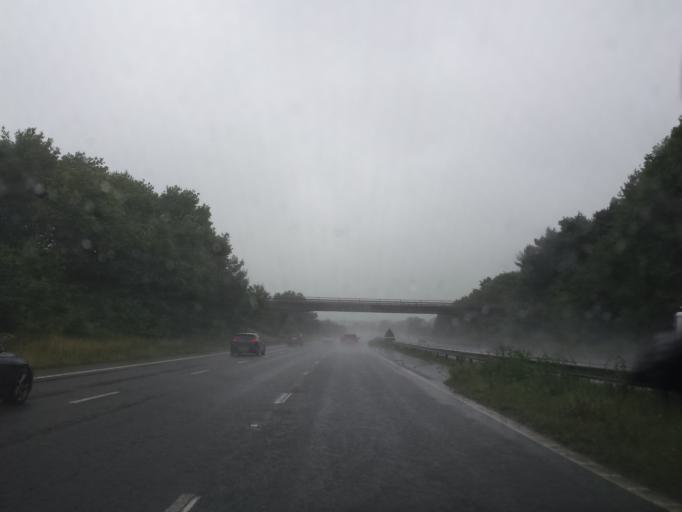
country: GB
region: England
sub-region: Leicestershire
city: Markfield
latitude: 52.6869
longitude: -1.2894
